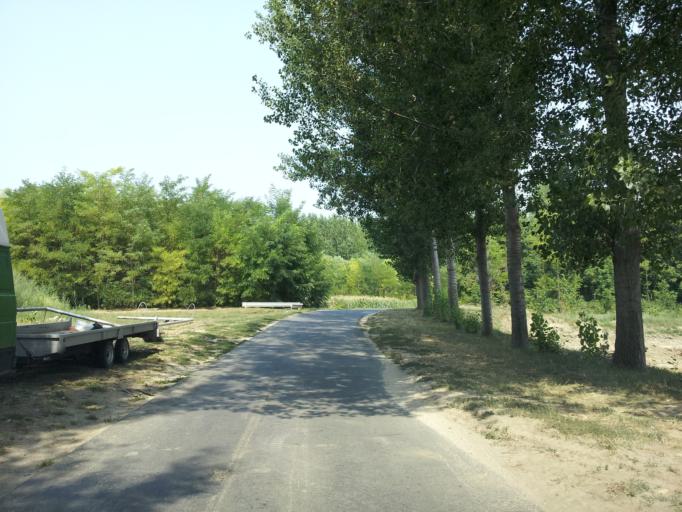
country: HU
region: Gyor-Moson-Sopron
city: Bakonyszentlaszlo
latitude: 47.4555
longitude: 17.7938
